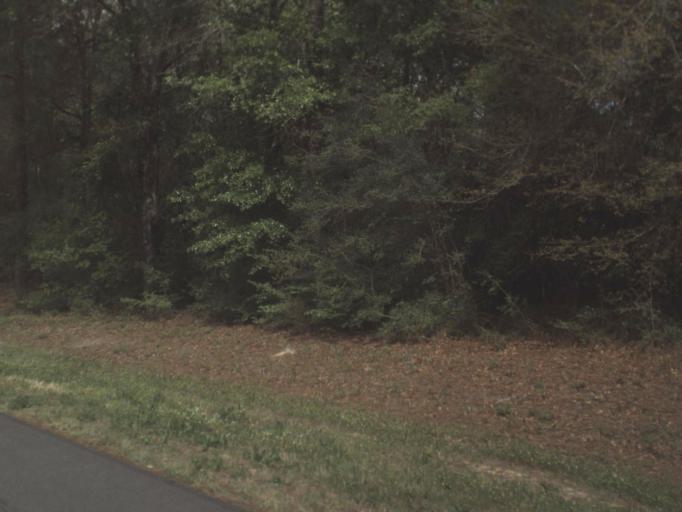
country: US
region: Alabama
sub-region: Covington County
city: Florala
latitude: 30.9333
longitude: -86.4793
